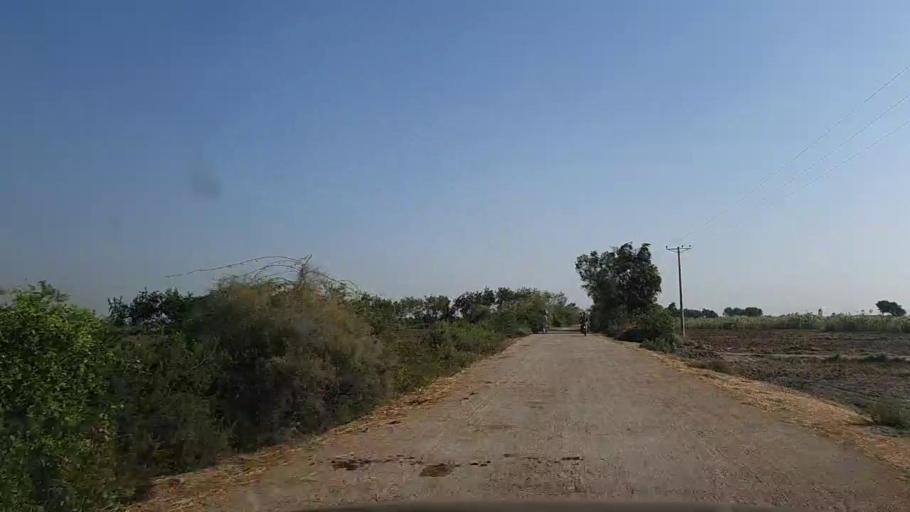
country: PK
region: Sindh
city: Daro Mehar
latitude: 24.6331
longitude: 68.0775
